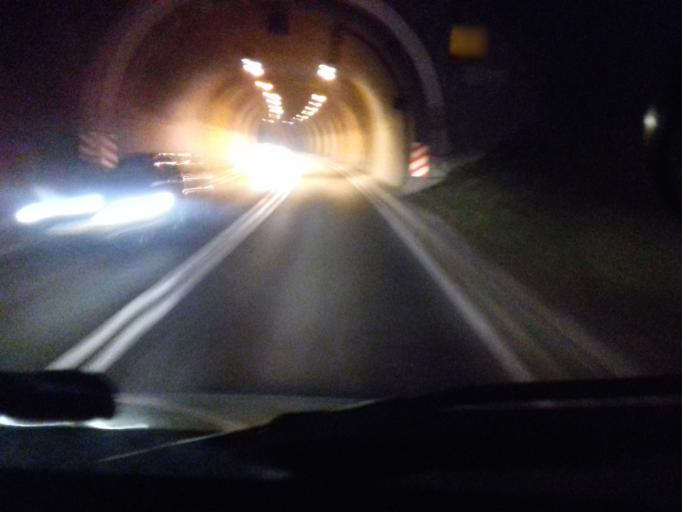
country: BA
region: Federation of Bosnia and Herzegovina
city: Zeljezno Polje
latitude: 44.3034
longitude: 17.9089
